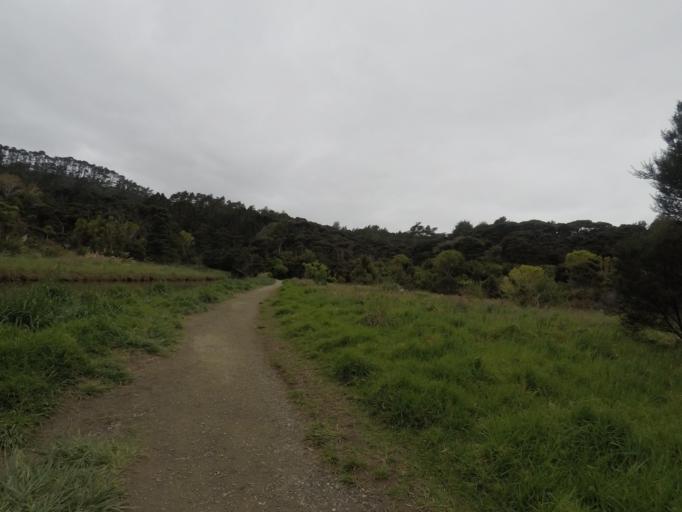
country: NZ
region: Auckland
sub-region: Auckland
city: Titirangi
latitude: -37.0013
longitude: 174.5925
